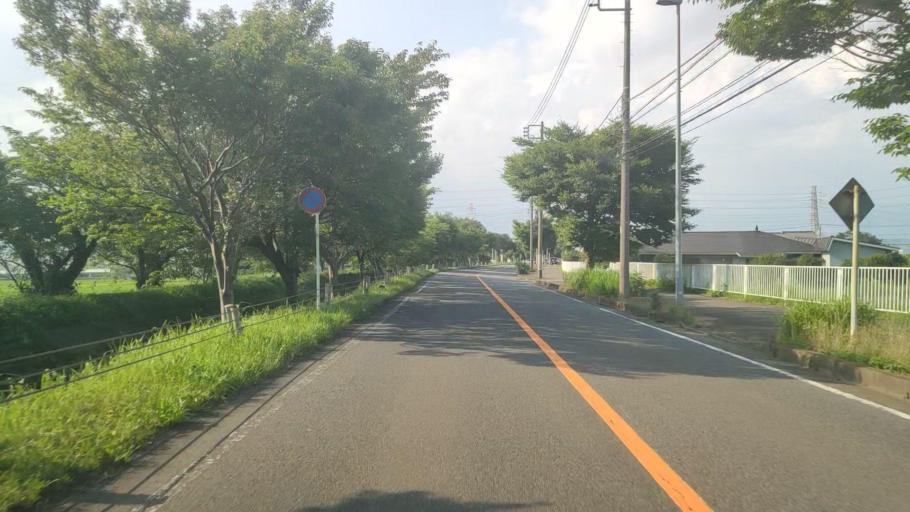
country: JP
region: Kanagawa
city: Isehara
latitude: 35.3938
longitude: 139.3379
